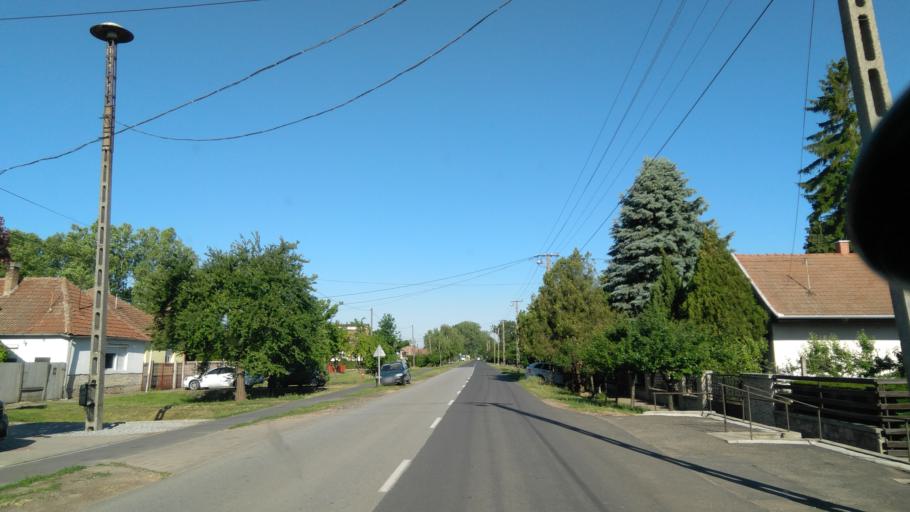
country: HU
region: Bekes
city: Elek
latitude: 46.5327
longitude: 21.2374
